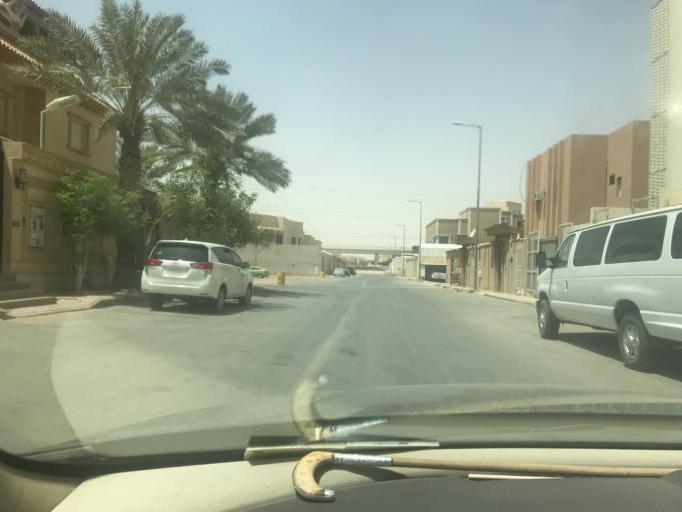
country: SA
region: Ar Riyad
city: Riyadh
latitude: 24.7982
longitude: 46.6965
